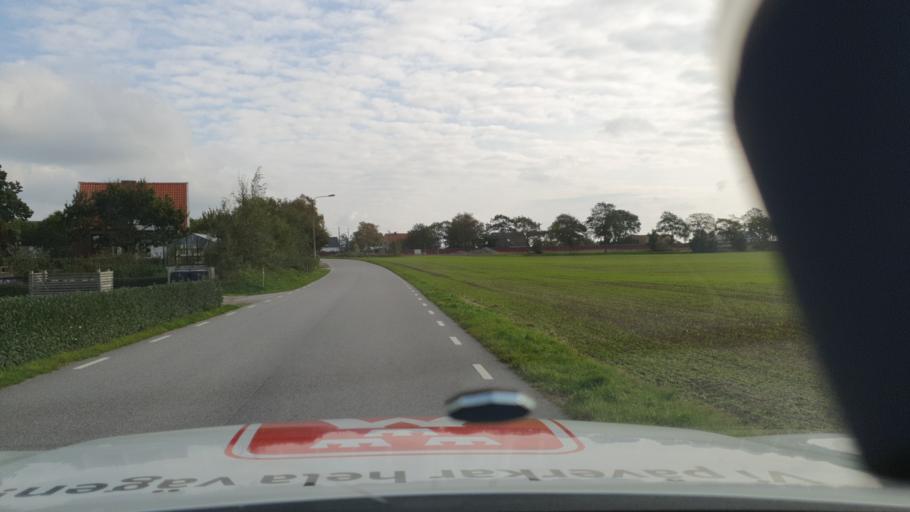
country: SE
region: Skane
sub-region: Trelleborgs Kommun
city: Trelleborg
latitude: 55.4133
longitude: 13.1495
